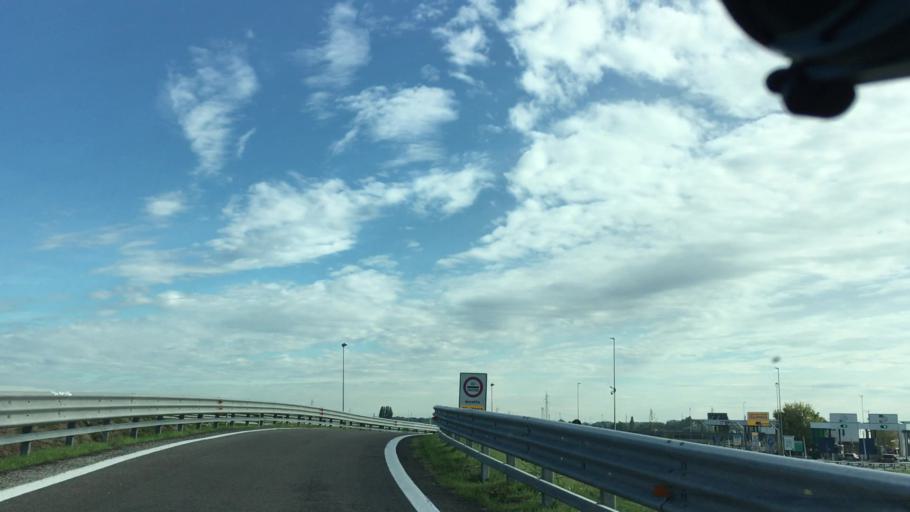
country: IT
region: Emilia-Romagna
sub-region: Provincia di Ferrara
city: Porotto-Cassama
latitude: 44.8656
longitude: 11.5707
